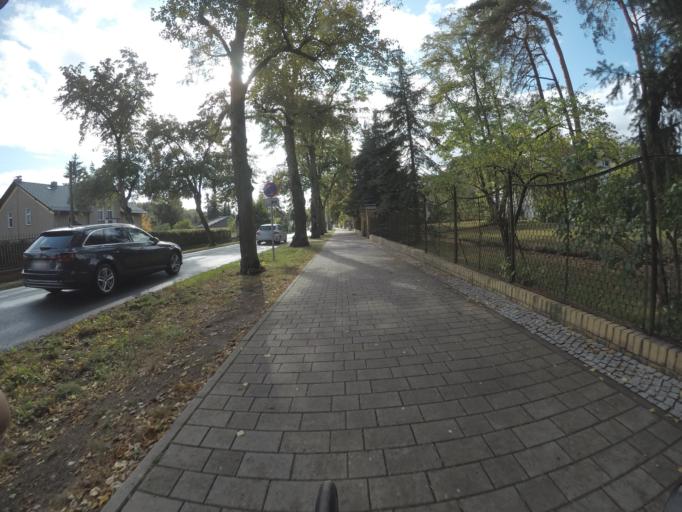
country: DE
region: Brandenburg
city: Rehfelde
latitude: 52.5368
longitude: 13.8497
